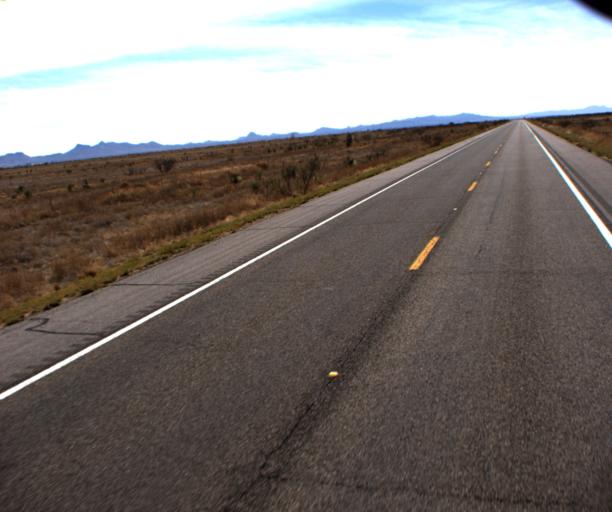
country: US
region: Arizona
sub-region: Cochise County
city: Pirtleville
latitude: 31.4652
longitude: -109.6161
